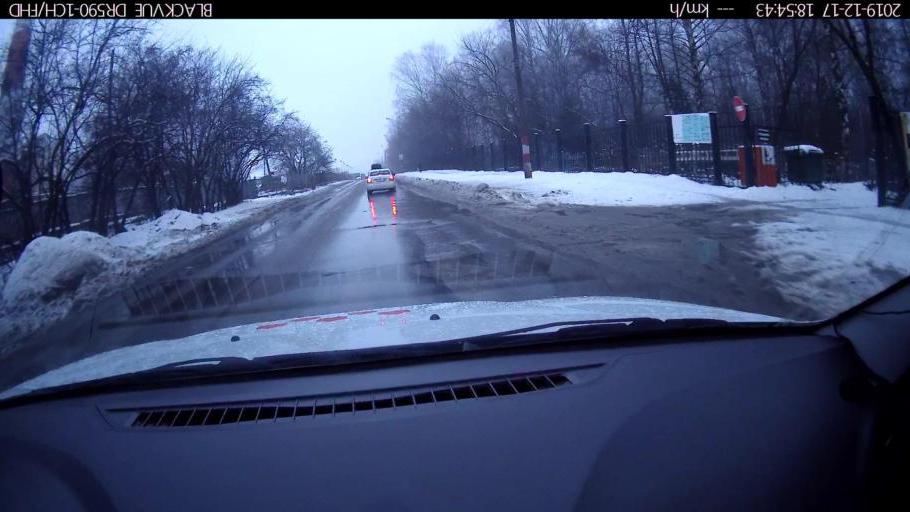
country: RU
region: Nizjnij Novgorod
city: Nizhniy Novgorod
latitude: 56.2826
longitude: 43.9982
